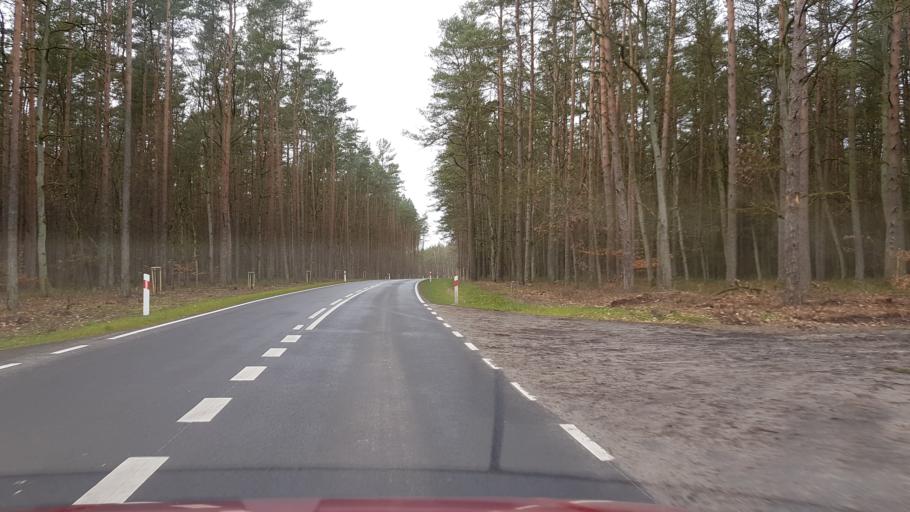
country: PL
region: West Pomeranian Voivodeship
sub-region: Powiat policki
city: Police
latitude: 53.6574
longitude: 14.4724
